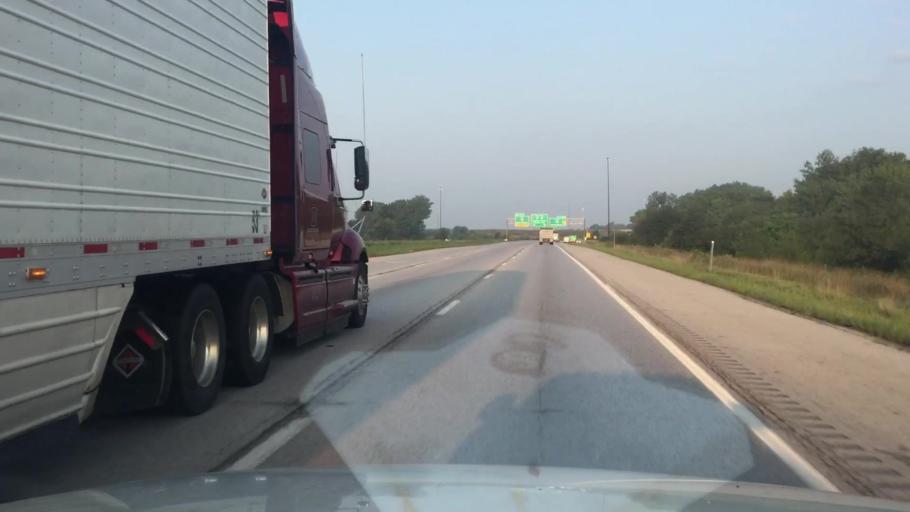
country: US
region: Iowa
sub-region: Polk County
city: Des Moines
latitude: 41.6539
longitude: -93.5649
